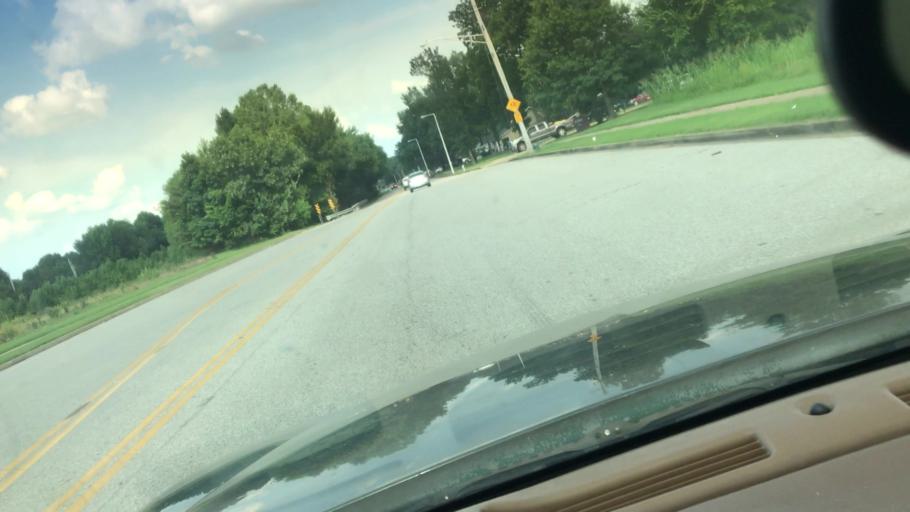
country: US
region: Tennessee
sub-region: Shelby County
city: Bartlett
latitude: 35.1941
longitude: -89.8142
